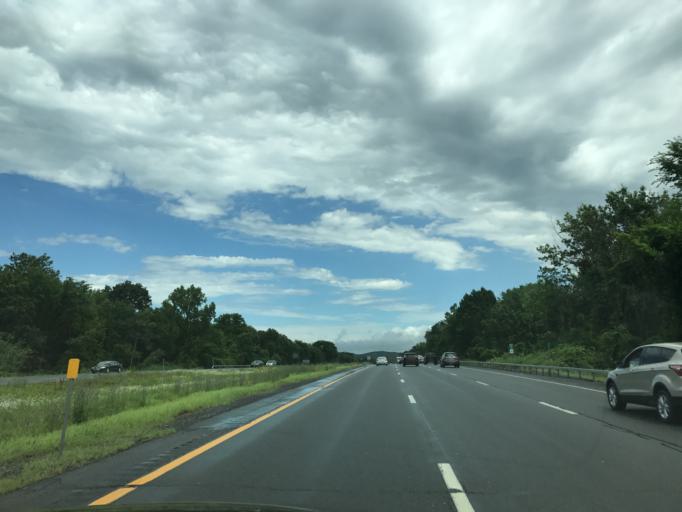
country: US
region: New York
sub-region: Albany County
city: Cohoes
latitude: 42.7790
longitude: -73.7596
